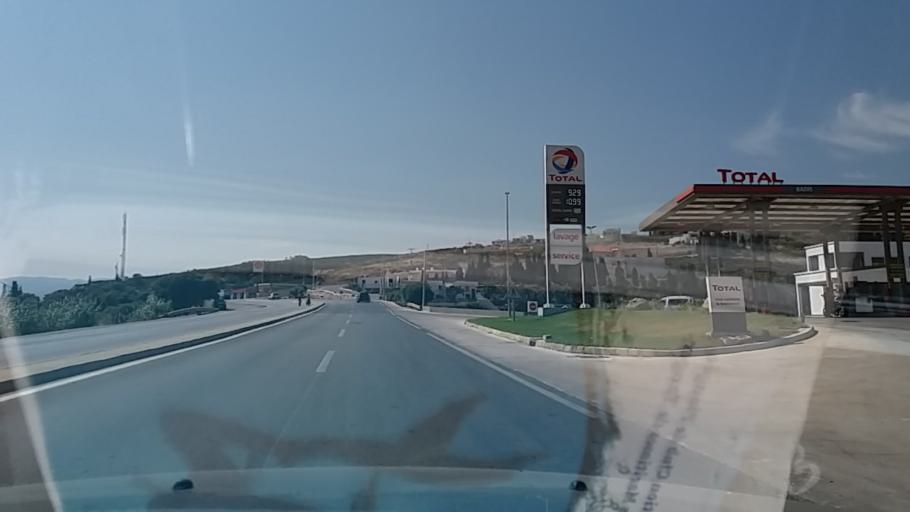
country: MA
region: Tanger-Tetouan
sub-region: Tetouan
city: Saddina
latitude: 35.5599
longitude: -5.4438
